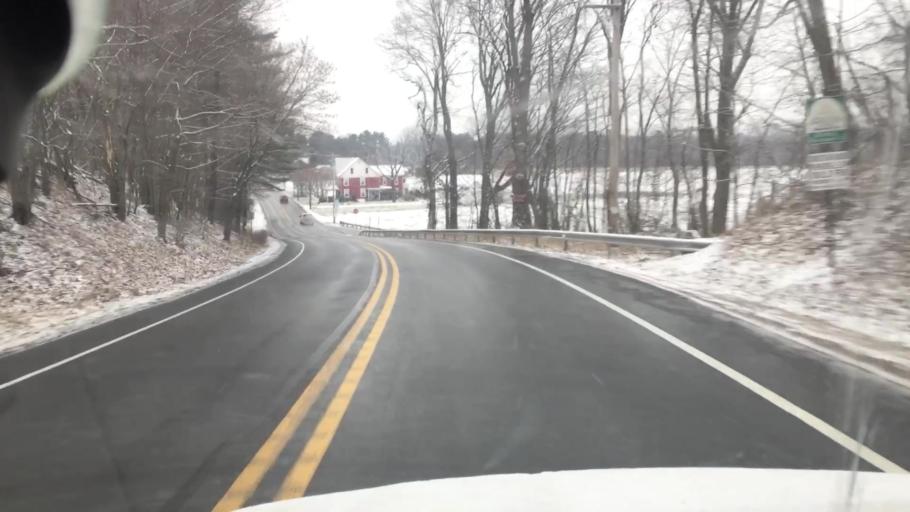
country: US
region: Pennsylvania
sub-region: Luzerne County
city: Nescopeck
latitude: 41.0549
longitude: -76.2014
